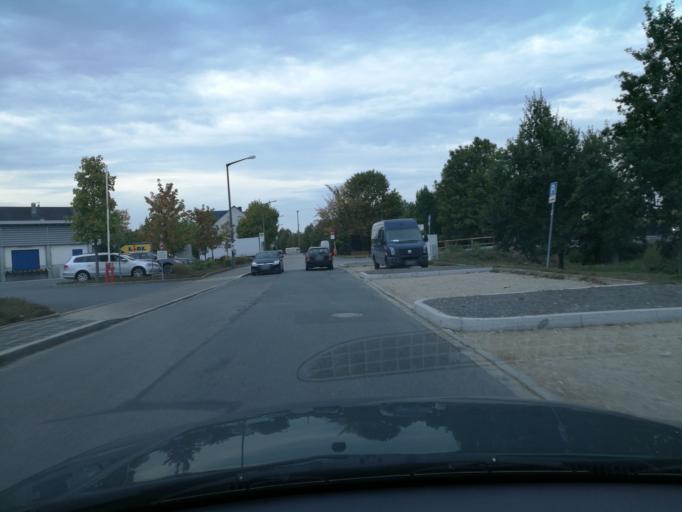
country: DE
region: Bavaria
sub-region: Regierungsbezirk Mittelfranken
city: Furth
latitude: 49.5235
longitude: 11.0150
